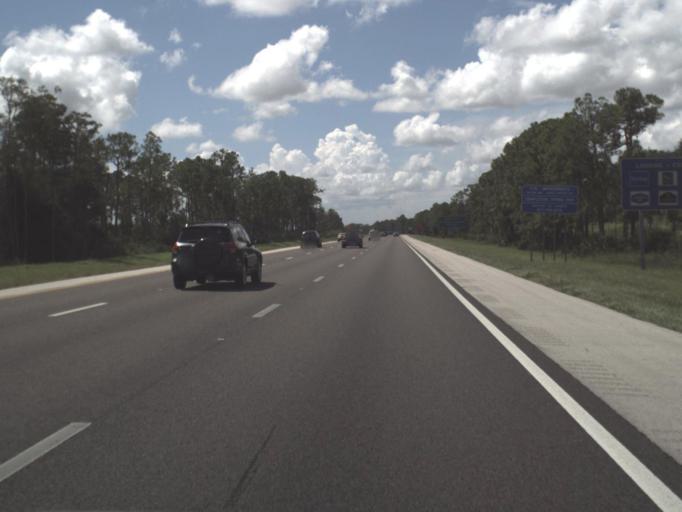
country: US
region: Florida
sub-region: Lee County
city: Gateway
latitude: 26.5625
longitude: -81.7943
